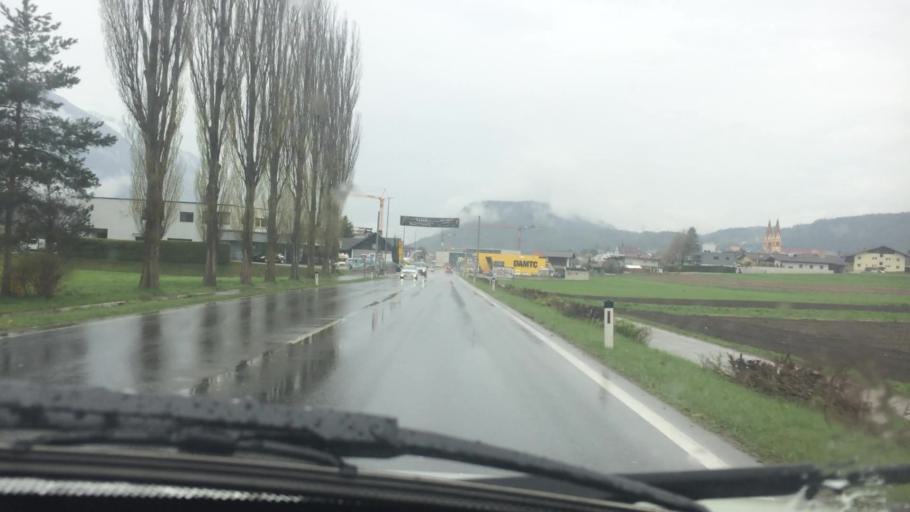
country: AT
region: Tyrol
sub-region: Politischer Bezirk Innsbruck Land
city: Pfaffenhofen
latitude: 47.3086
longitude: 11.0844
